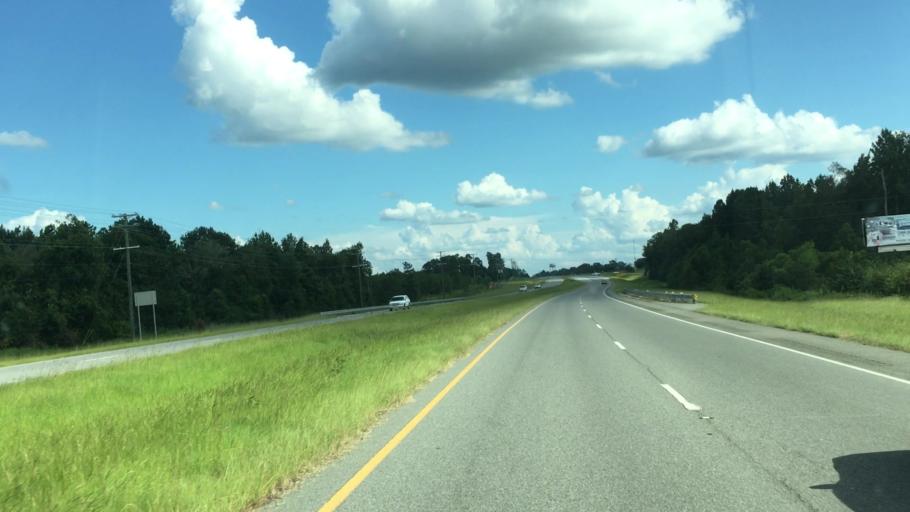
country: US
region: Georgia
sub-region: Laurens County
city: Dublin
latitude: 32.5142
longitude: -82.9543
